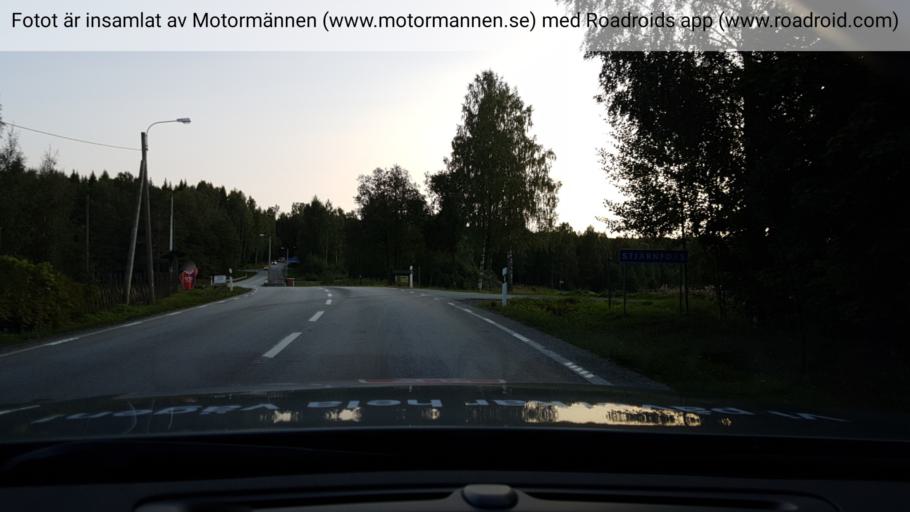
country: SE
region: OErebro
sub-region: Ljusnarsbergs Kommun
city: Kopparberg
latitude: 59.8336
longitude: 14.9999
